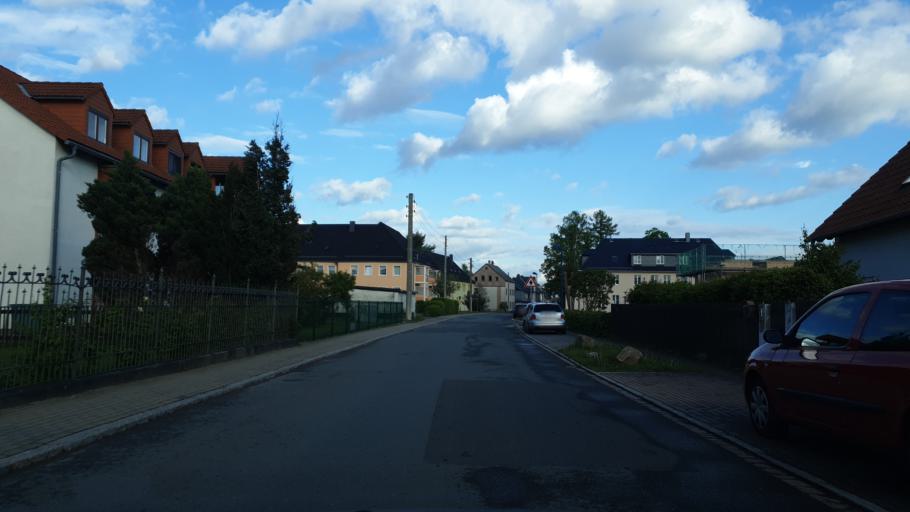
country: DE
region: Saxony
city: Lugau
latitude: 50.7243
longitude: 12.7304
